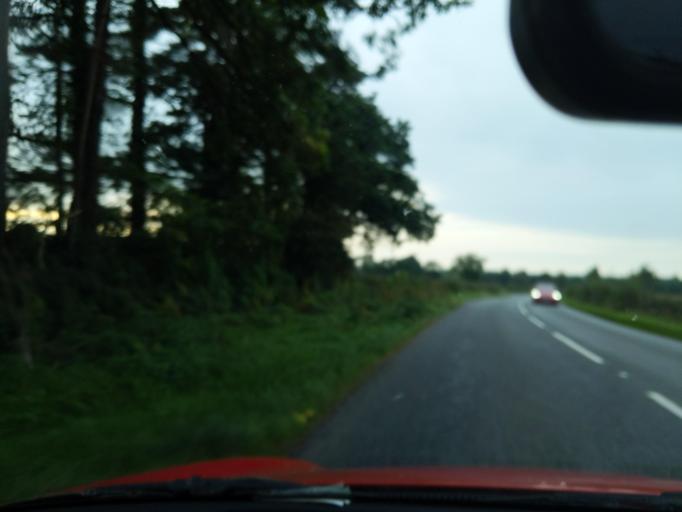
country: GB
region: England
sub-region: Devon
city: Okehampton
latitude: 50.8114
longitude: -4.0609
